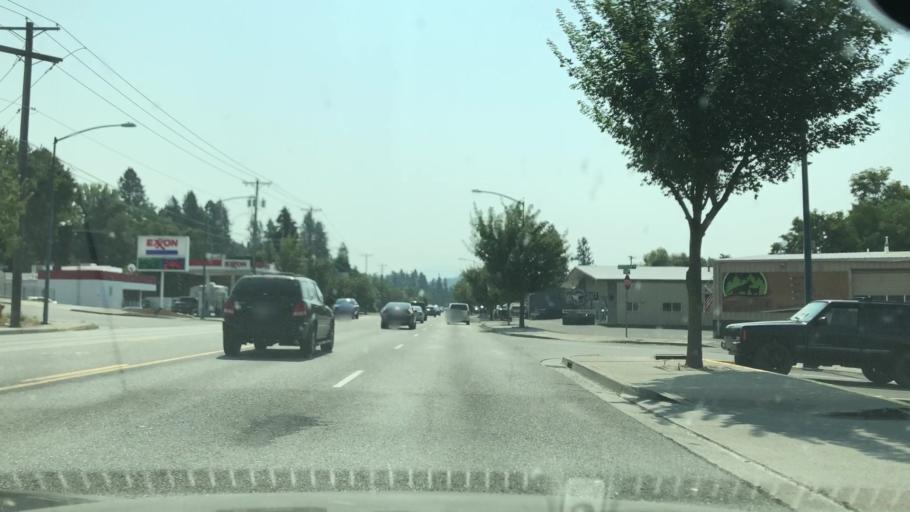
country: US
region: Idaho
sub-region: Kootenai County
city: Coeur d'Alene
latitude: 47.6920
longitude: -116.8017
